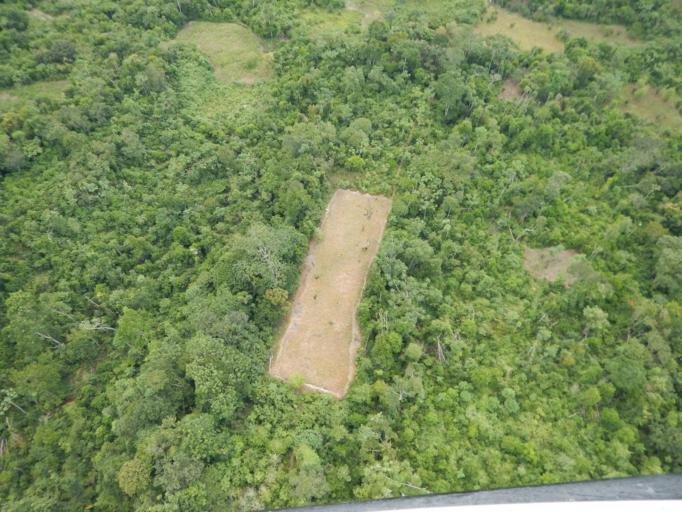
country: BO
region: Cochabamba
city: Chimore
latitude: -16.5376
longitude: -65.8408
